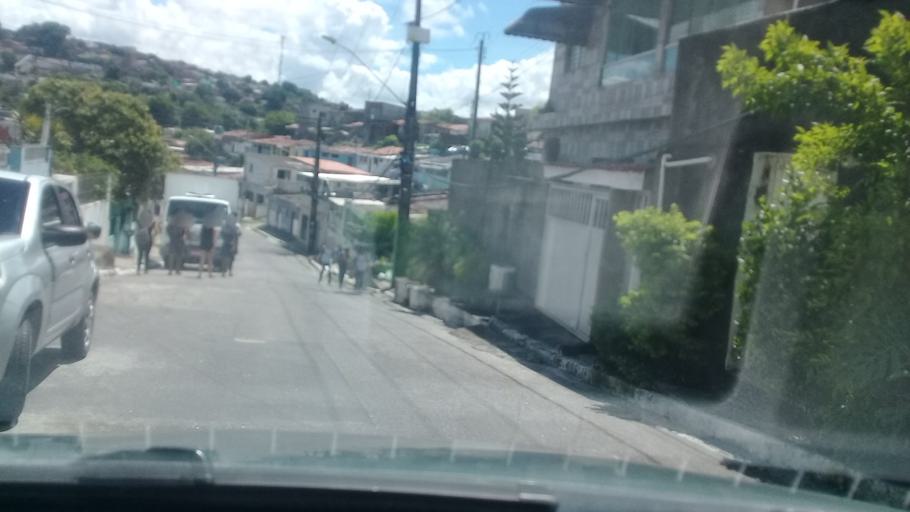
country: BR
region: Pernambuco
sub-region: Jaboatao Dos Guararapes
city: Jaboatao dos Guararapes
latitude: -8.1287
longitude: -34.9474
